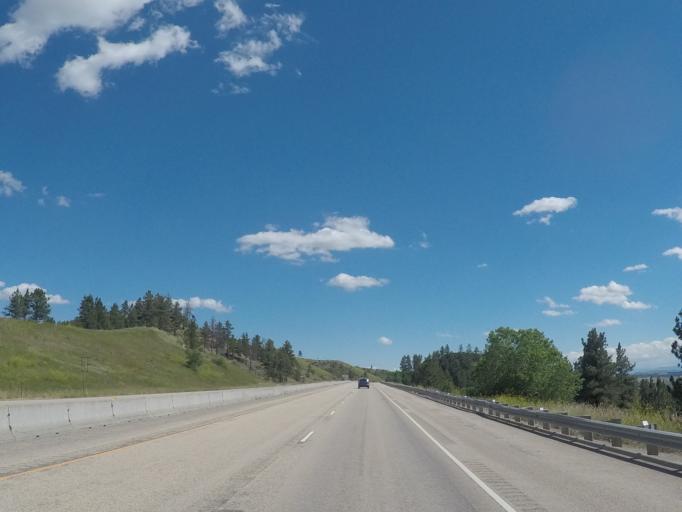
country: US
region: Montana
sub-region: Big Horn County
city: Crow Agency
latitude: 45.3393
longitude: -107.3525
